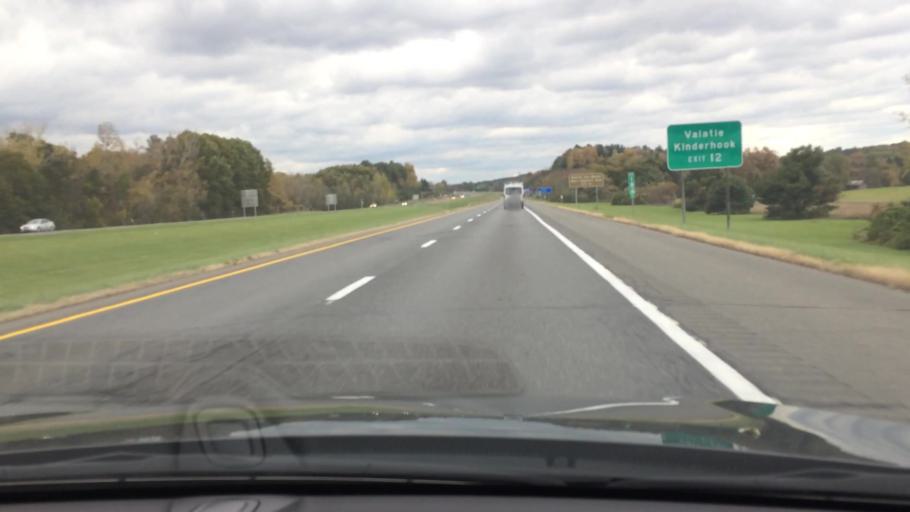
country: US
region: New York
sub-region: Rensselaer County
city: Castleton-on-Hudson
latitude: 42.5024
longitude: -73.6871
